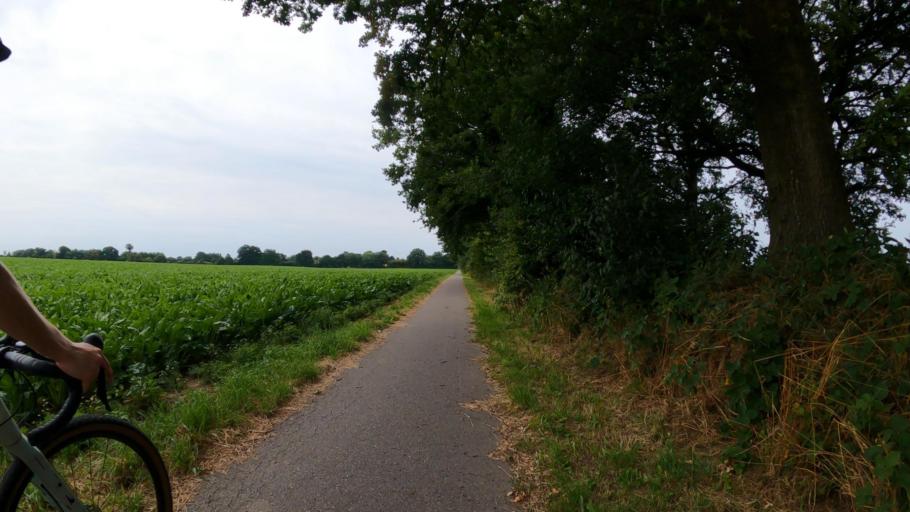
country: DE
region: Schleswig-Holstein
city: Leezen
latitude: 53.8686
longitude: 10.2349
